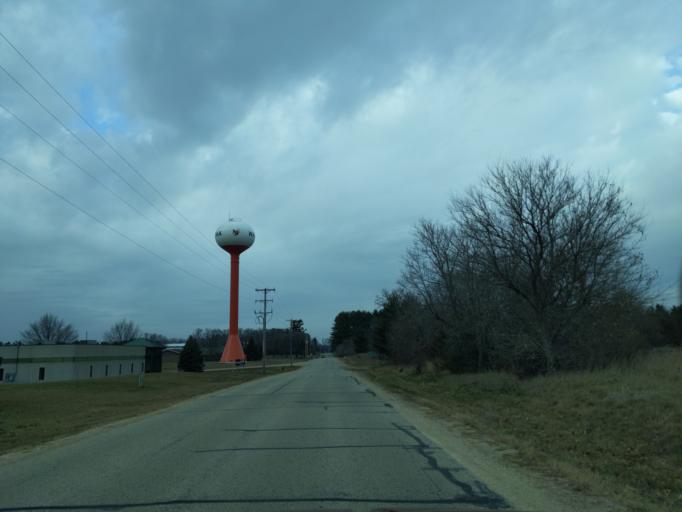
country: US
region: Wisconsin
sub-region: Waushara County
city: Wautoma
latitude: 44.0647
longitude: -89.2773
